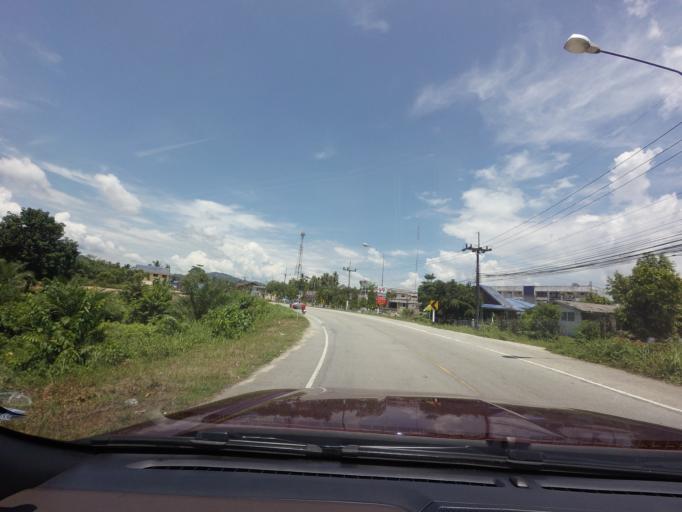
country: TH
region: Narathiwat
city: Chanae
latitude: 6.1317
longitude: 101.6974
